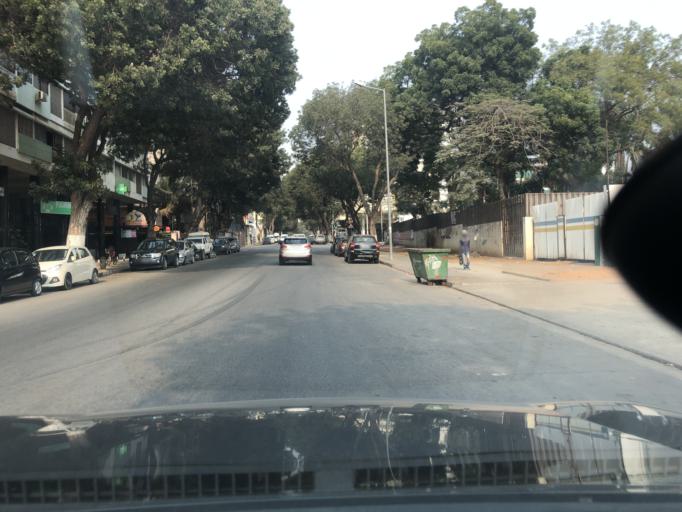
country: AO
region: Luanda
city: Luanda
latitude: -8.8186
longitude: 13.2420
